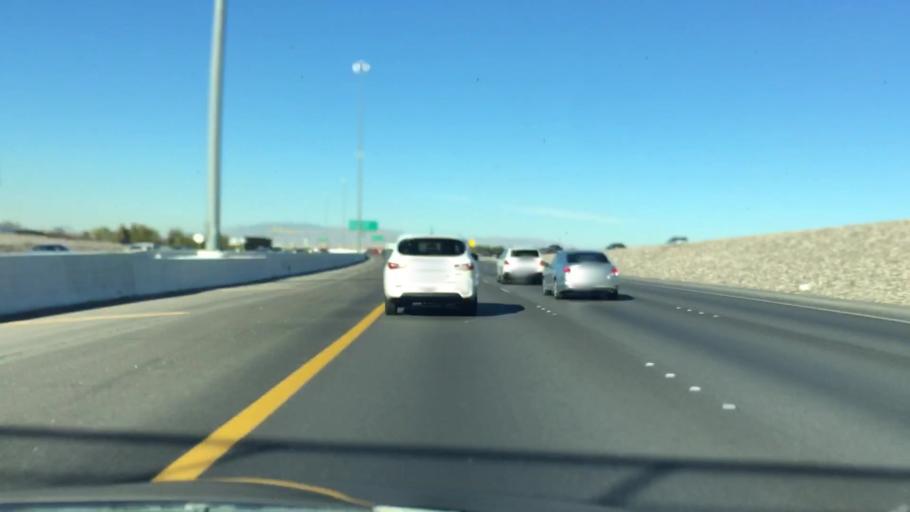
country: US
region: Nevada
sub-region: Clark County
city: Paradise
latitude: 36.0432
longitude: -115.1339
